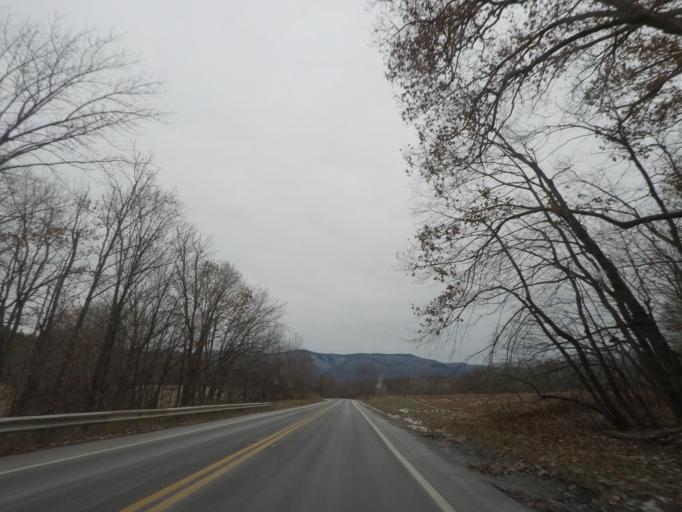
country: US
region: Massachusetts
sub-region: Berkshire County
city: Williamstown
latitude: 42.7036
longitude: -73.2402
